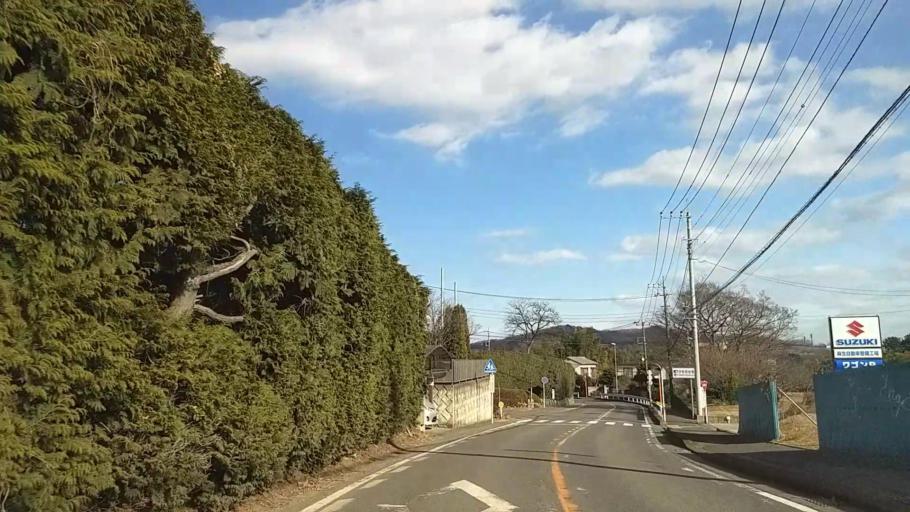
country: JP
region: Kanagawa
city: Isehara
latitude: 35.4192
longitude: 139.2885
